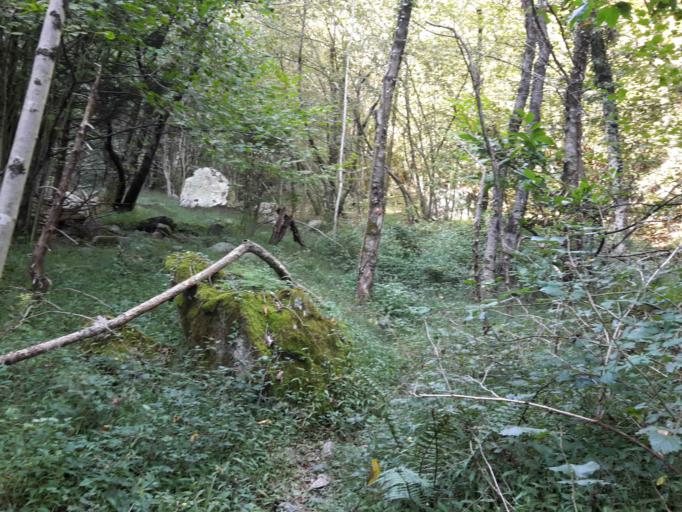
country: CH
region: Ticino
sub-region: Bellinzona District
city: Sementina
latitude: 46.1905
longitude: 8.9852
